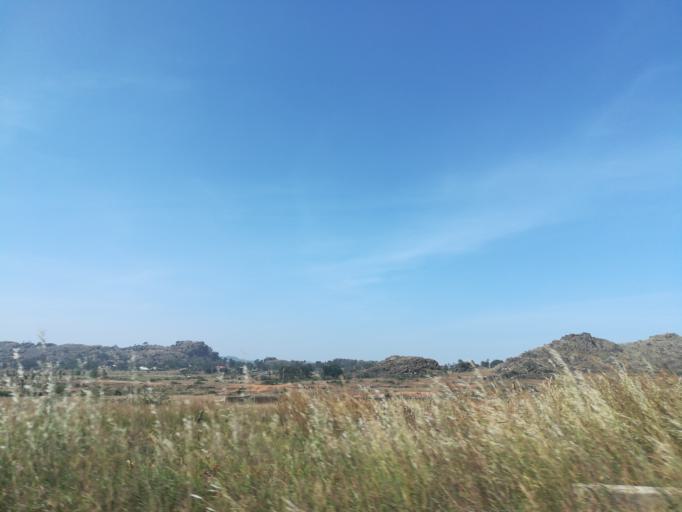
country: NG
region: Plateau
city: Bukuru
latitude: 9.7646
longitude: 8.9041
